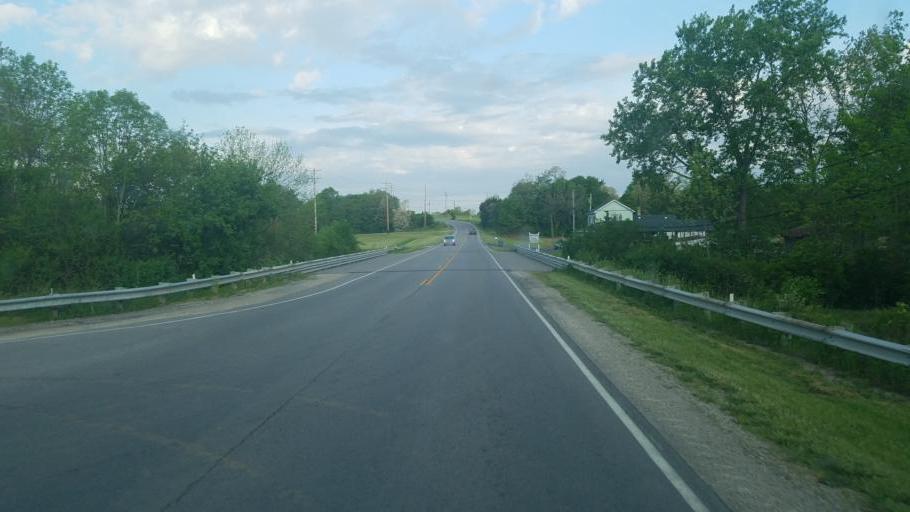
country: US
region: Ohio
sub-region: Highland County
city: Leesburg
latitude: 39.3471
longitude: -83.5836
